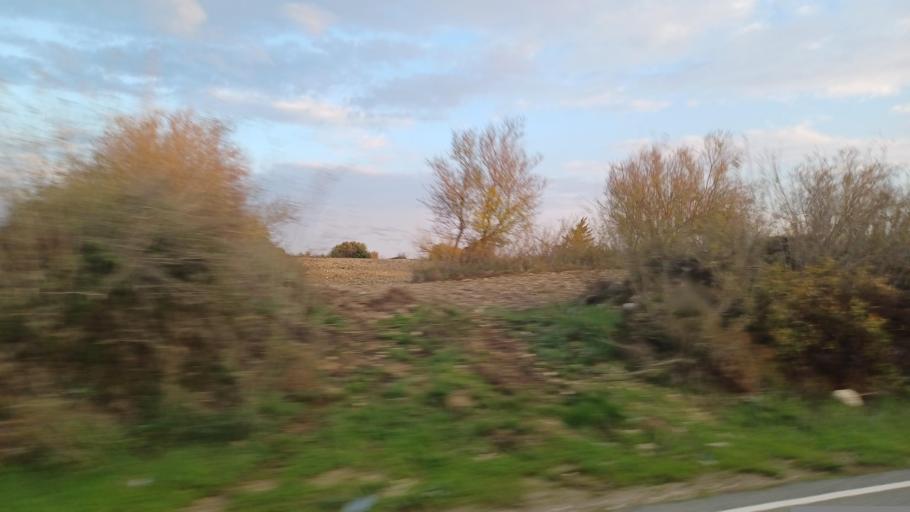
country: CY
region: Pafos
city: Pegeia
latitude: 34.9107
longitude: 32.4417
